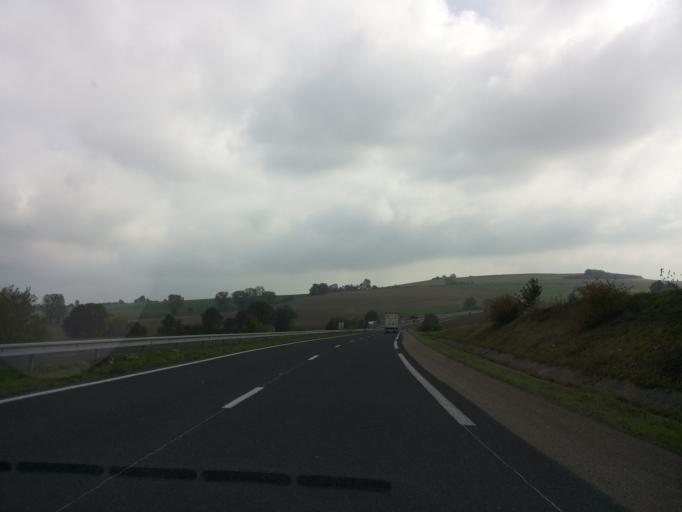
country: FR
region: Lorraine
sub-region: Departement de la Moselle
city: Solgne
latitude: 48.9468
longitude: 6.3145
